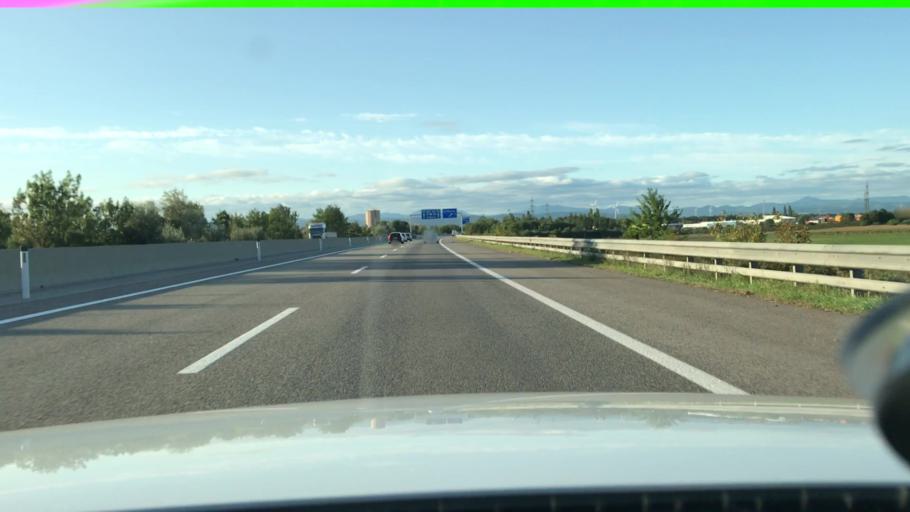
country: AT
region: Lower Austria
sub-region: Politischer Bezirk Sankt Polten
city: Herzogenburg
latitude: 48.2368
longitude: 15.6821
